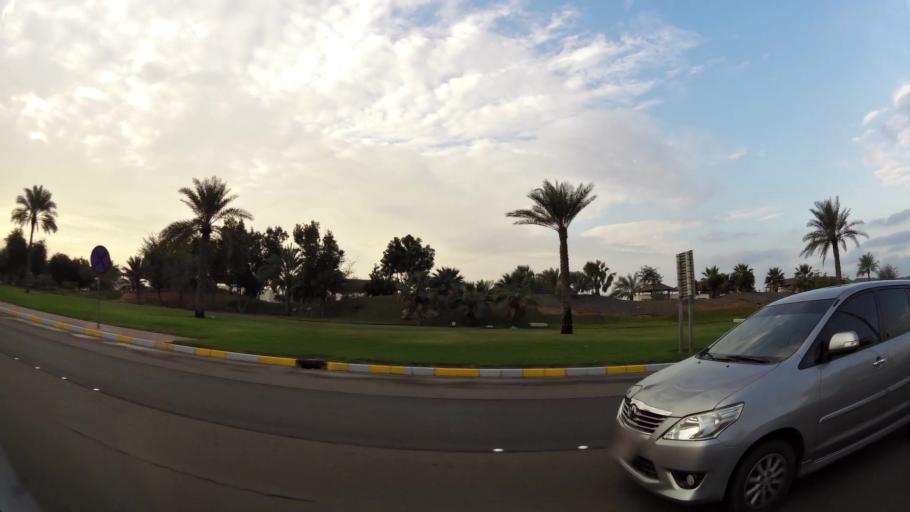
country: AE
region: Abu Dhabi
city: Abu Dhabi
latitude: 24.4241
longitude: 54.4111
